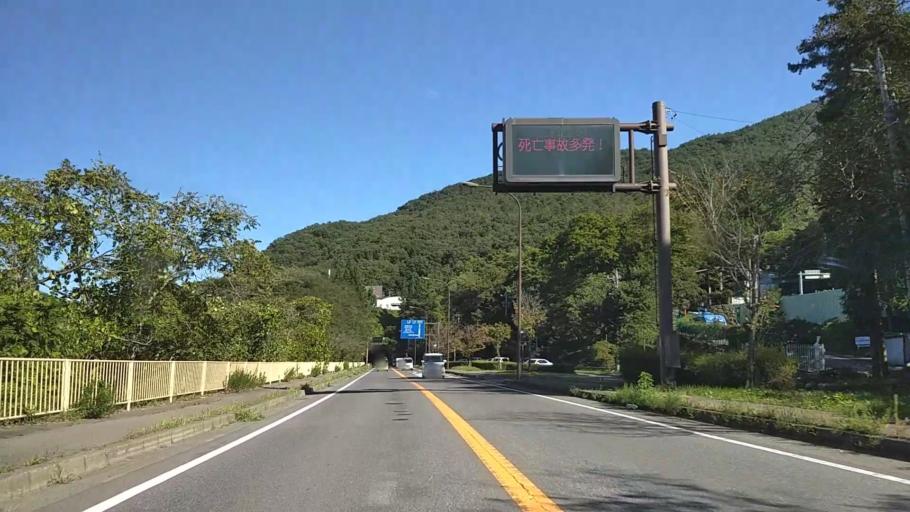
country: JP
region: Nagano
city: Nagano-shi
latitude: 36.6206
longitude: 138.1080
